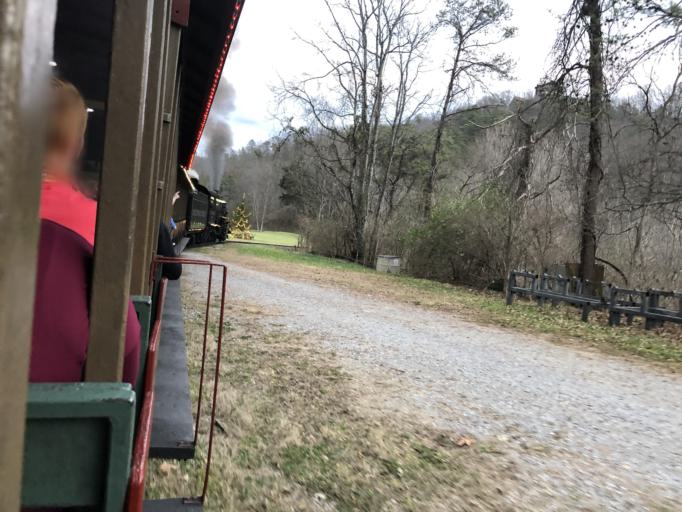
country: US
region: Tennessee
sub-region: Sevier County
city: Pigeon Forge
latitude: 35.7949
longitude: -83.5271
